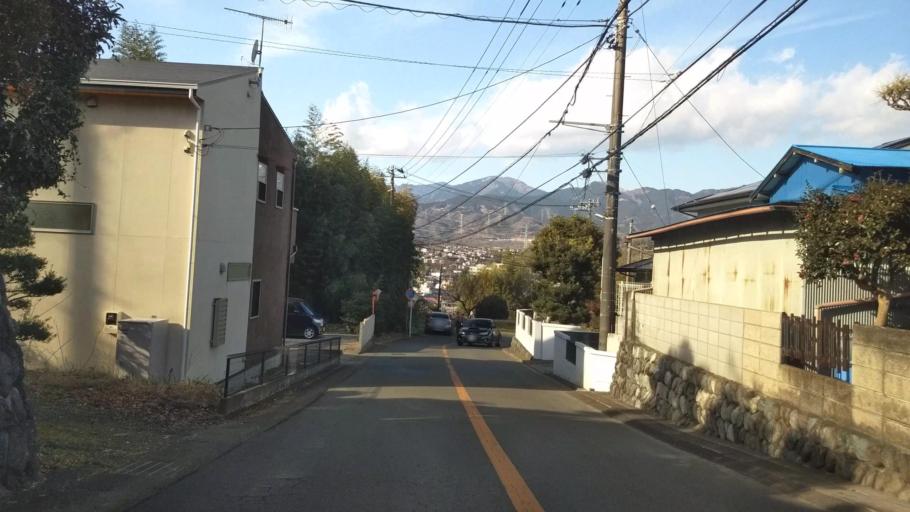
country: JP
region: Kanagawa
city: Hadano
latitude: 35.3781
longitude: 139.2454
